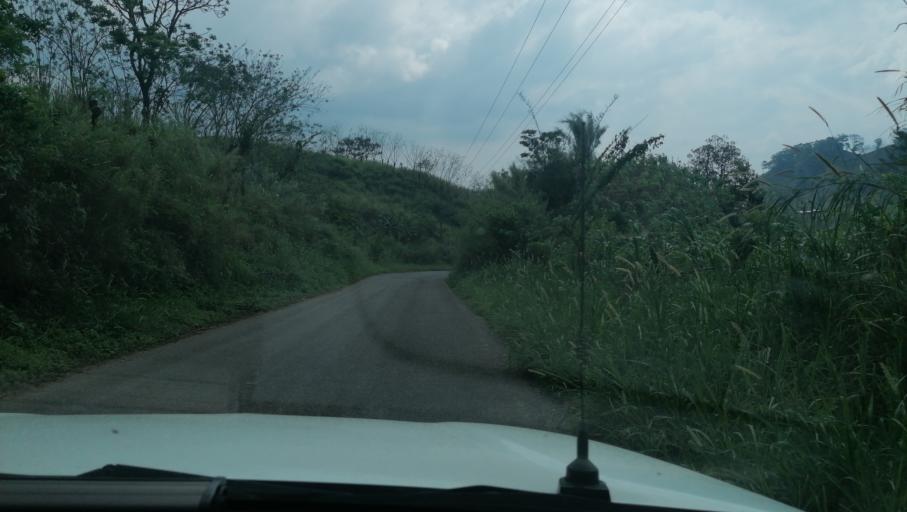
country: MX
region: Chiapas
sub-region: Francisco Leon
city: San Miguel la Sardina
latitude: 17.2361
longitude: -93.3254
